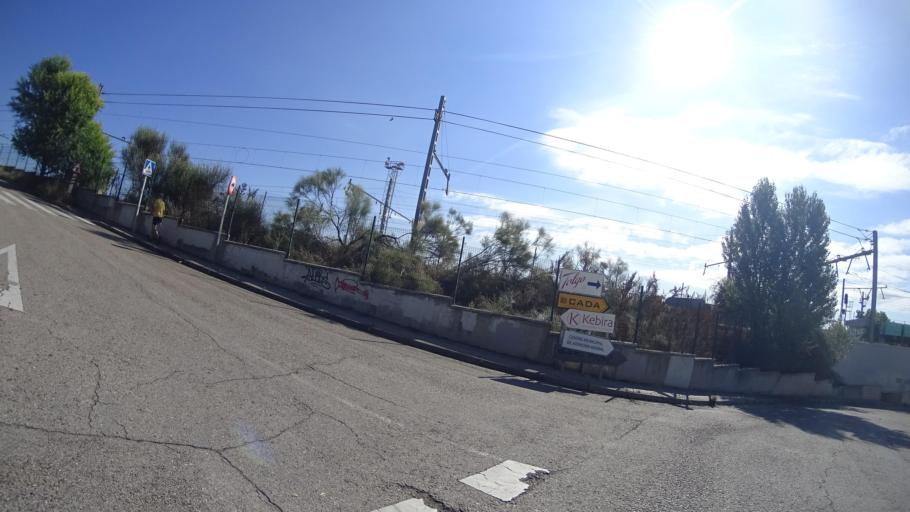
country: ES
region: Madrid
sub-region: Provincia de Madrid
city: Las Matas
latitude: 40.5388
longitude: -3.8893
